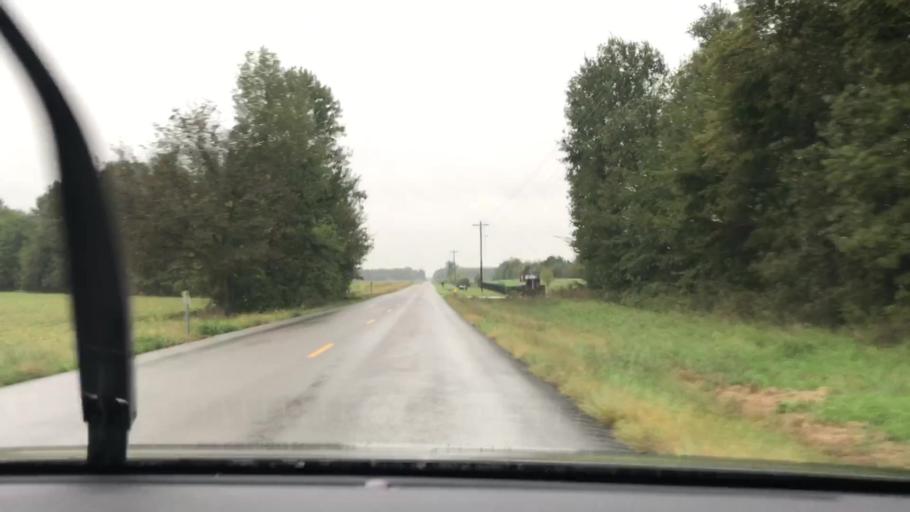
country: US
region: Kentucky
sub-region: Hopkins County
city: Madisonville
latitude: 37.3665
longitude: -87.3644
